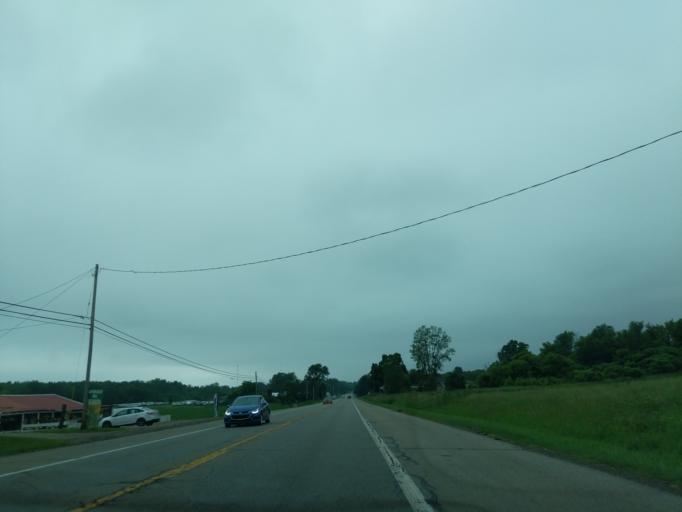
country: US
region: Michigan
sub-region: Branch County
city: Quincy
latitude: 41.9390
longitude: -84.9221
